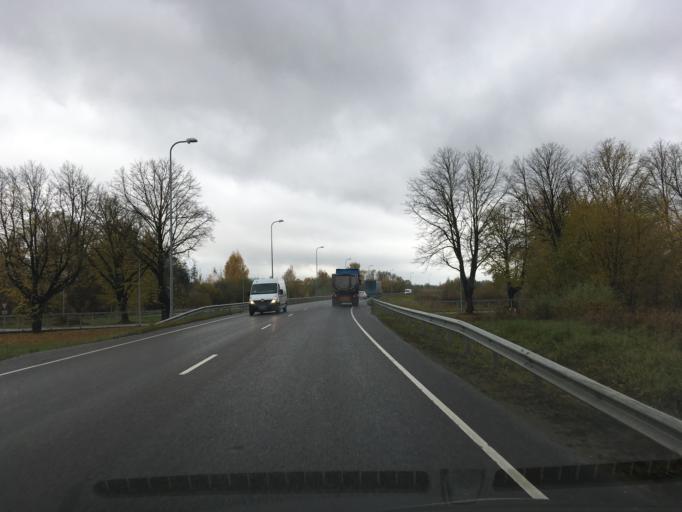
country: EE
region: Paernumaa
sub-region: Paernu linn
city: Parnu
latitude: 58.3992
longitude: 24.4694
